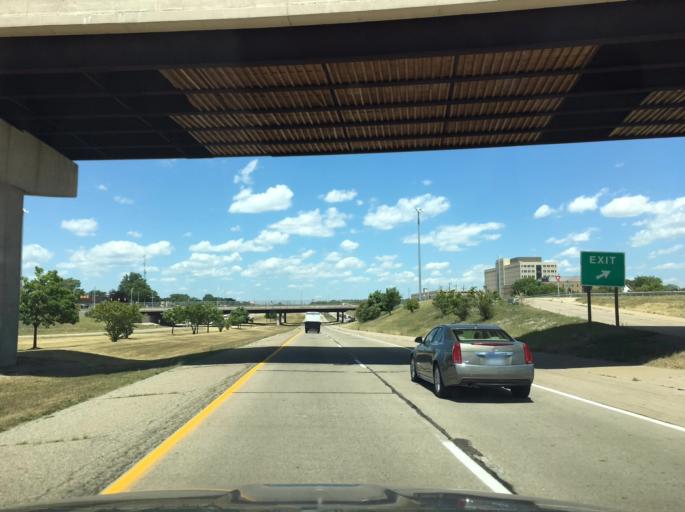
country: US
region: Michigan
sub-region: Macomb County
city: Center Line
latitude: 42.4891
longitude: -83.0455
